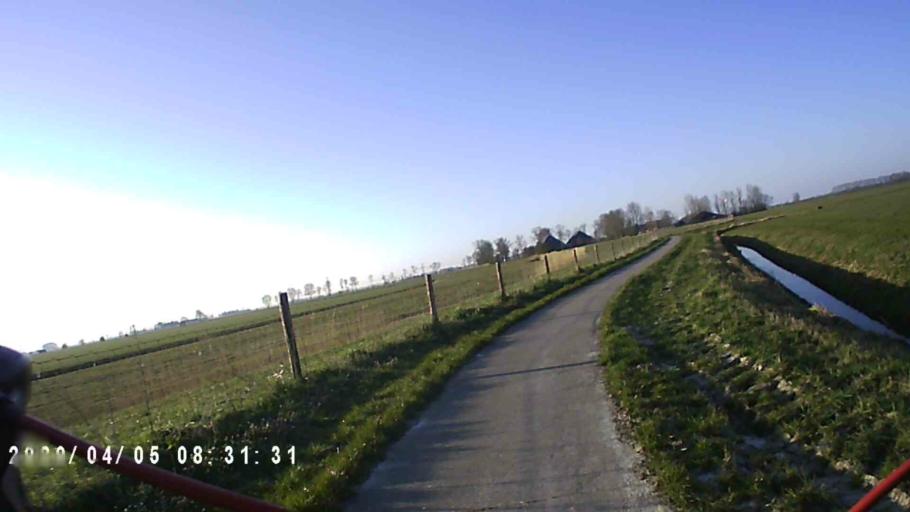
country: NL
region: Groningen
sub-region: Gemeente Winsum
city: Winsum
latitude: 53.3292
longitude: 6.4864
